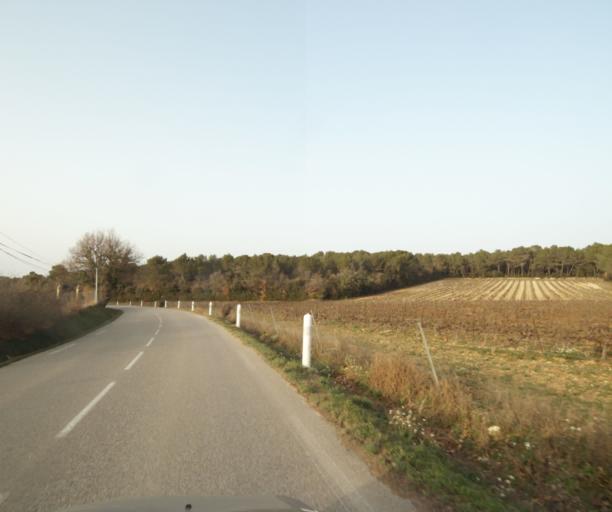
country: FR
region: Provence-Alpes-Cote d'Azur
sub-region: Departement des Bouches-du-Rhone
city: Rognes
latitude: 43.6367
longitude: 5.3611
